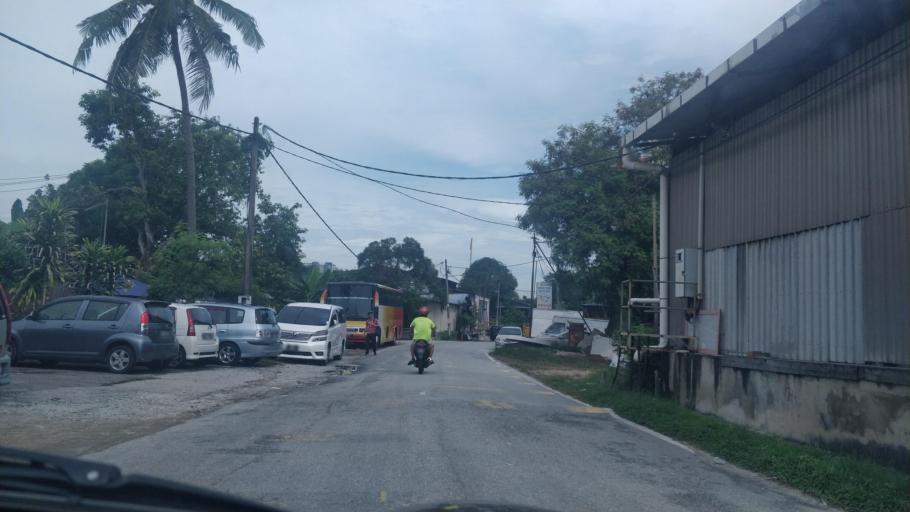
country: MY
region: Selangor
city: Kuang
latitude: 3.2015
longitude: 101.5940
